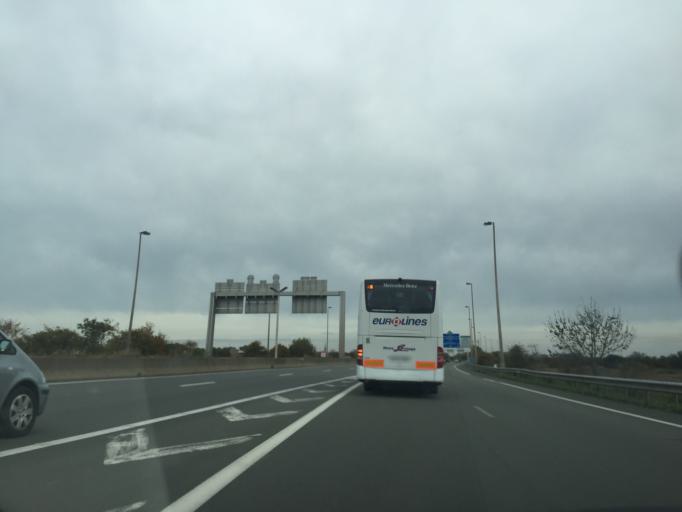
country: FR
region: Nord-Pas-de-Calais
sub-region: Departement du Pas-de-Calais
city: Coquelles
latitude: 50.9416
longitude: 1.8219
